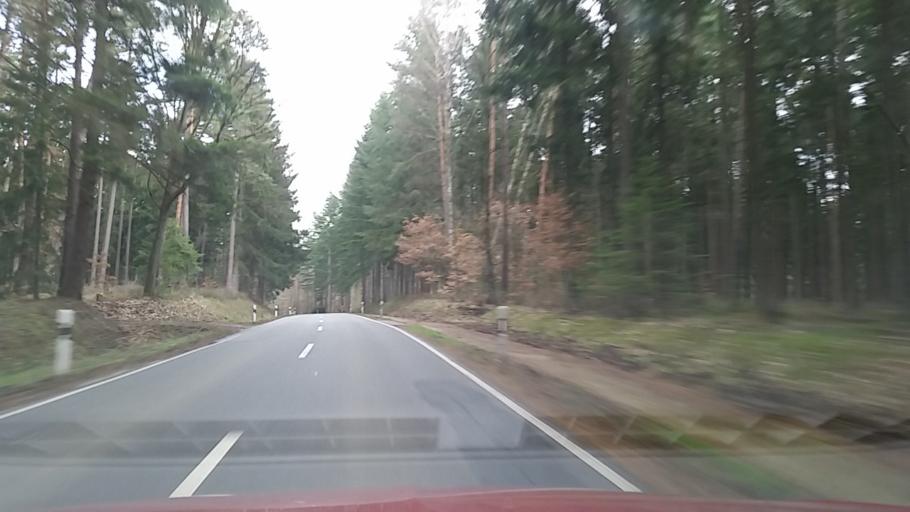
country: DE
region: Lower Saxony
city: Zernien
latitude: 53.0882
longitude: 10.9450
